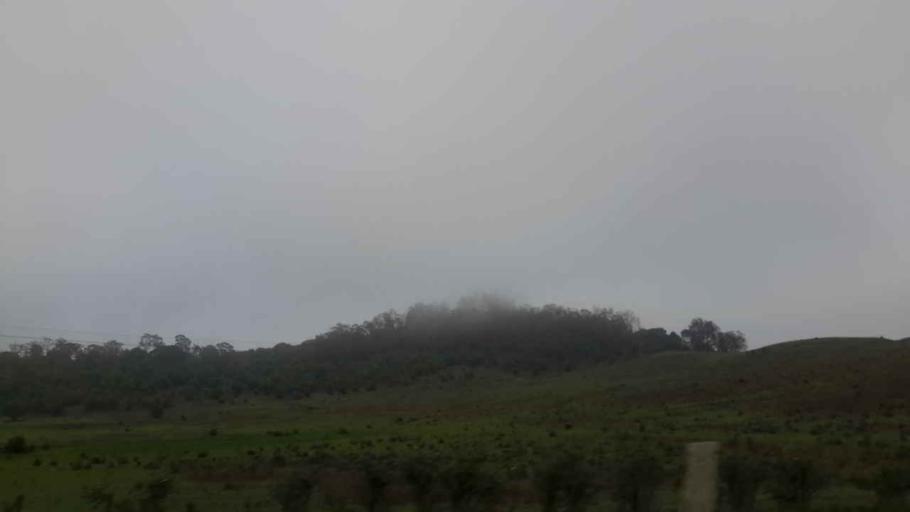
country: AU
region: New South Wales
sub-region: Camden
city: Camden South
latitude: -34.1209
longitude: 150.6989
